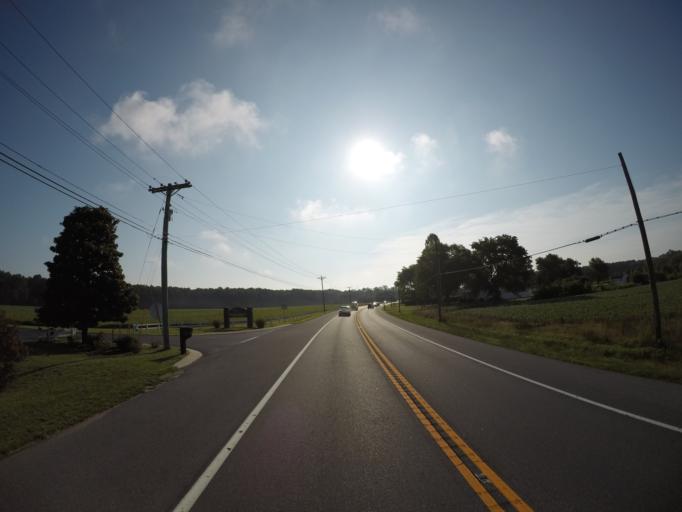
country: US
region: Delaware
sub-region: Sussex County
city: Georgetown
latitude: 38.6987
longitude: -75.4506
